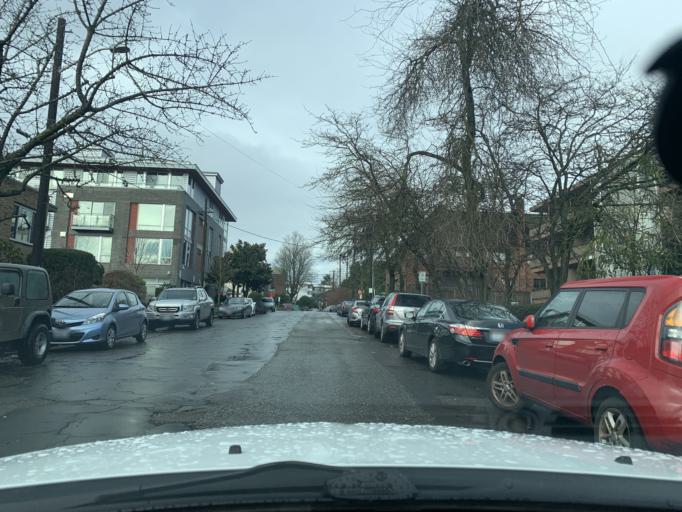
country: US
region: Washington
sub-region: King County
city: Seattle
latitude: 47.6192
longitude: -122.3143
